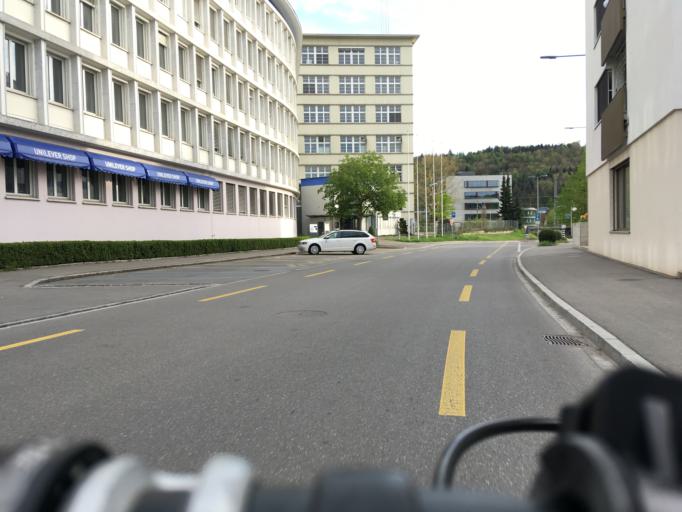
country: CH
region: Schaffhausen
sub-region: Bezirk Reiat
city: Thayngen
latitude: 47.7468
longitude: 8.7071
